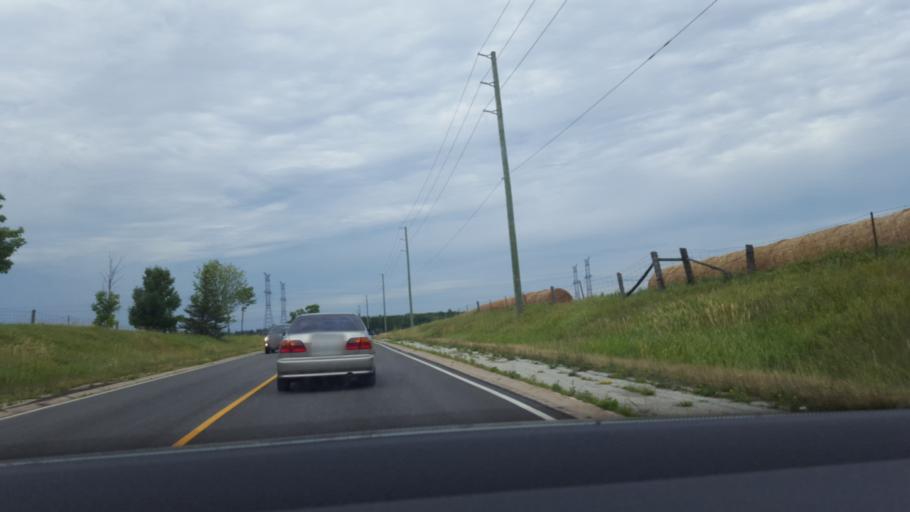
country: CA
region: Ontario
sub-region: Halton
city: Milton
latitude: 43.5598
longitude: -79.8998
